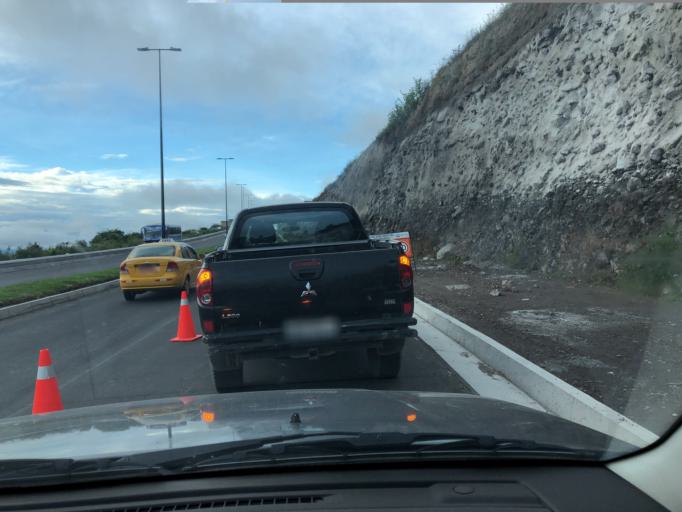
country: EC
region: Imbabura
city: Ibarra
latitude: 0.3488
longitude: -78.1411
